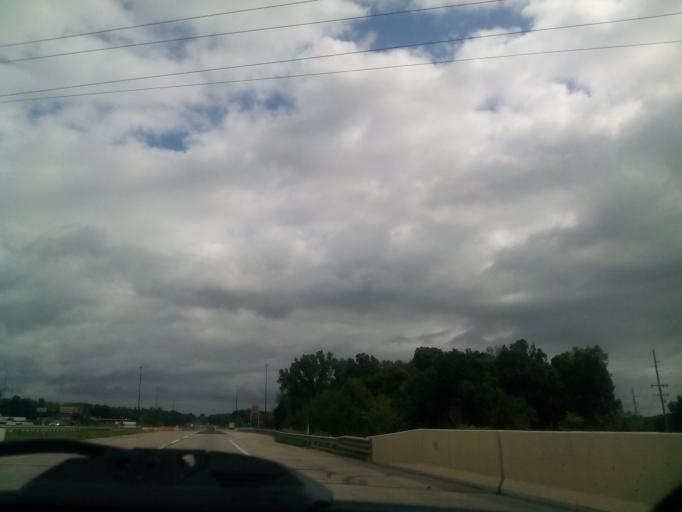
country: US
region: Indiana
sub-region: Steuben County
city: Fremont
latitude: 41.7302
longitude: -84.9710
